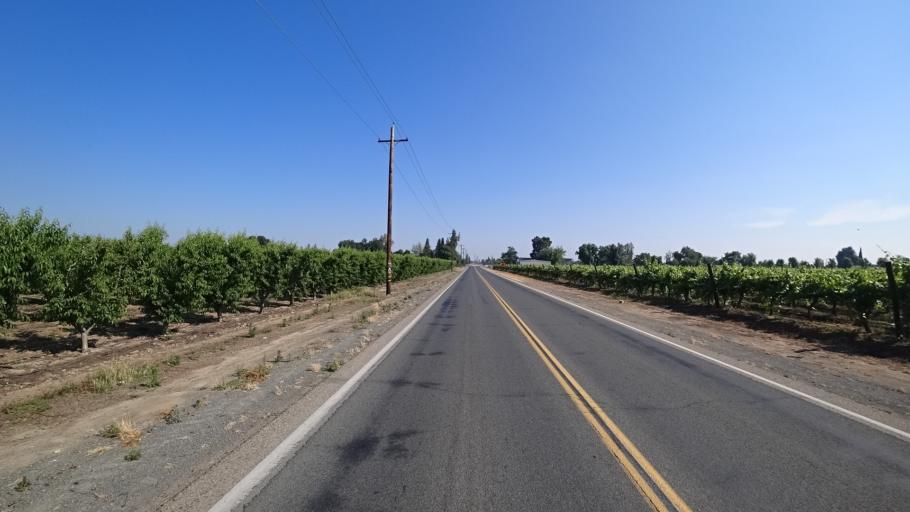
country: US
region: California
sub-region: Fresno County
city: Kingsburg
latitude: 36.4863
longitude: -119.5573
